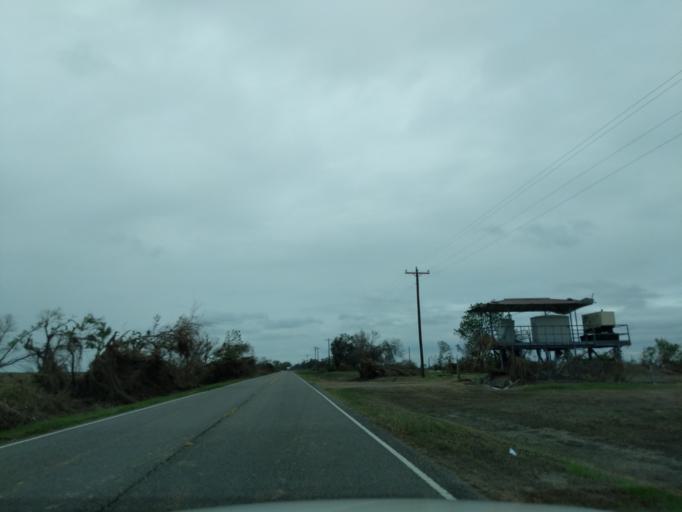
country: US
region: Louisiana
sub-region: Cameron Parish
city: Cameron
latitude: 29.7867
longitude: -93.1295
